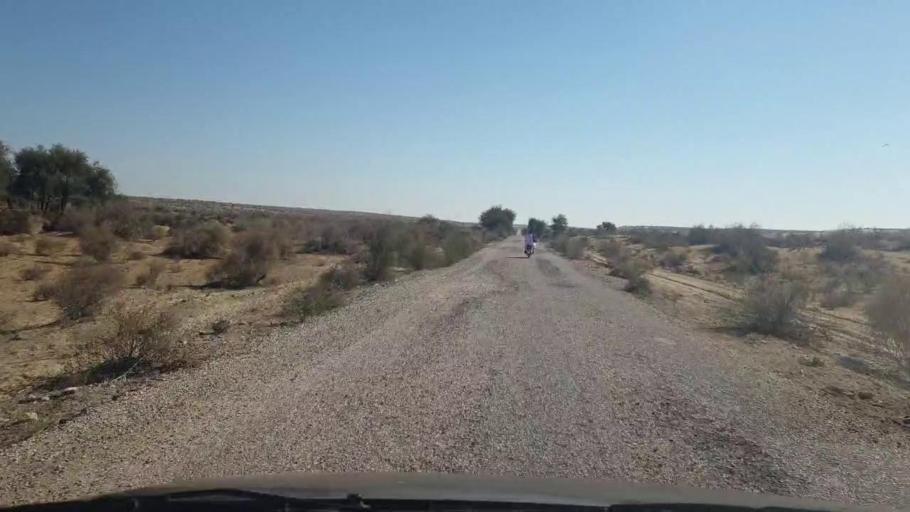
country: PK
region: Sindh
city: Bozdar
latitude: 27.0351
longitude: 68.6977
